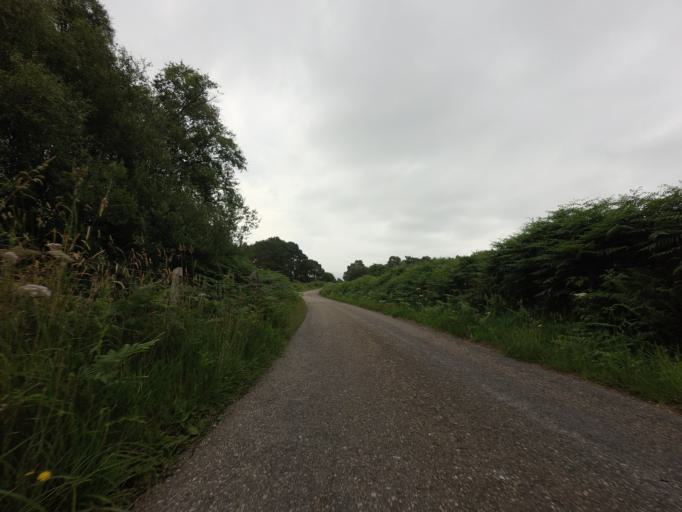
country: GB
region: Scotland
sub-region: Highland
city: Evanton
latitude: 57.9052
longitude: -4.3905
